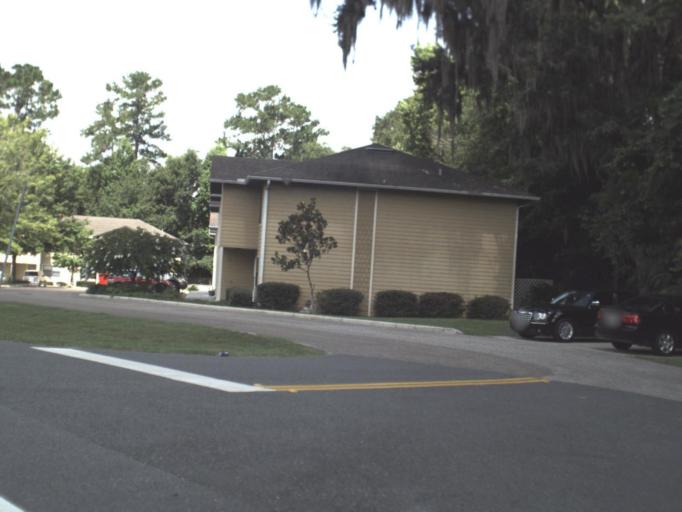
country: US
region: Florida
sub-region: Alachua County
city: Alachua
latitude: 29.8033
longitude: -82.4924
